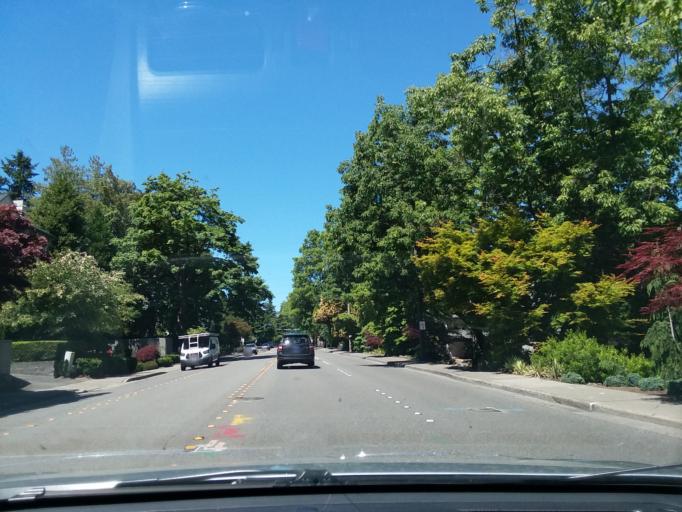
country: US
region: Washington
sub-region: King County
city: Bellevue
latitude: 47.6157
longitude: -122.2070
